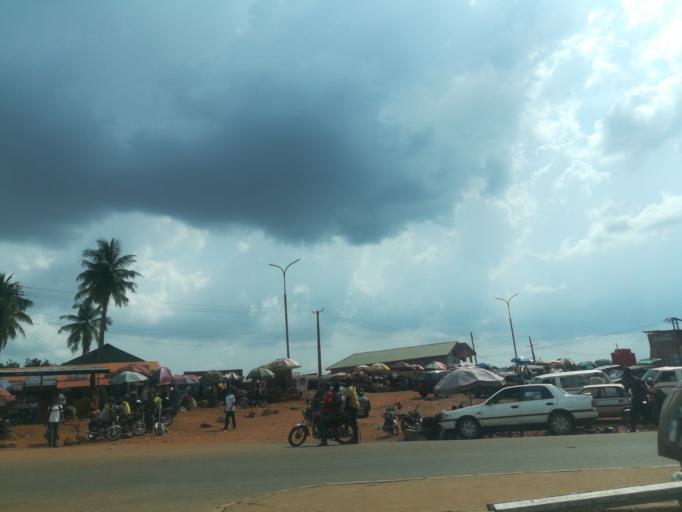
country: NG
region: Oyo
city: Moniya
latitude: 7.4709
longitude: 3.9160
